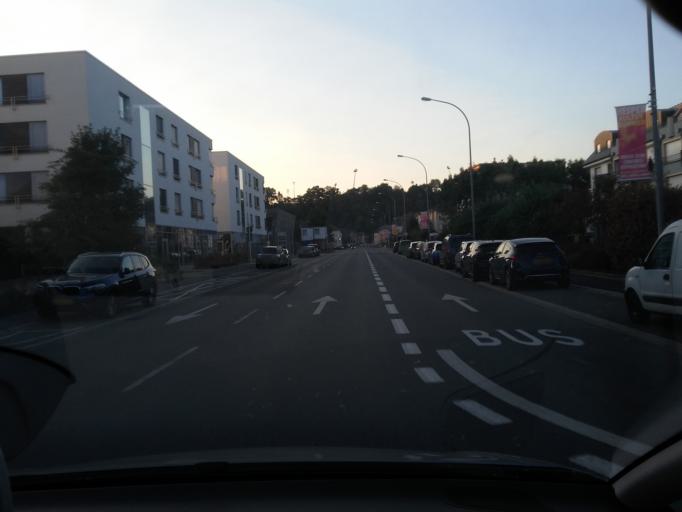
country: LU
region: Luxembourg
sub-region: Canton de Luxembourg
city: Alzingen
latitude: 49.5703
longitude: 6.1606
